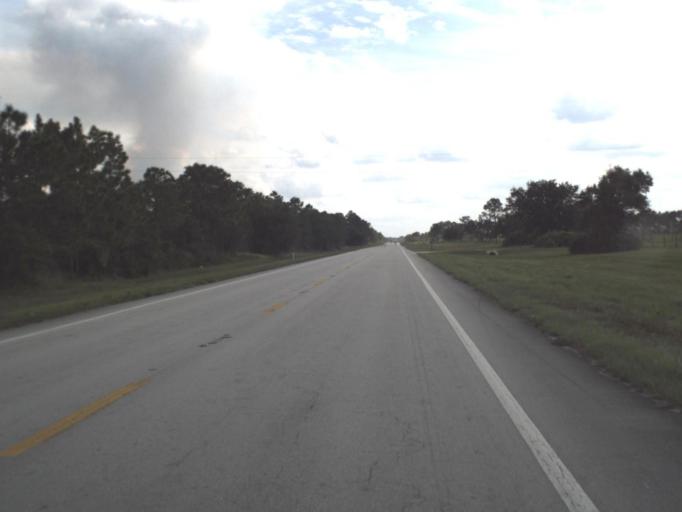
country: US
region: Florida
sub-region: Indian River County
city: Fellsmere
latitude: 27.6187
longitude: -80.8598
